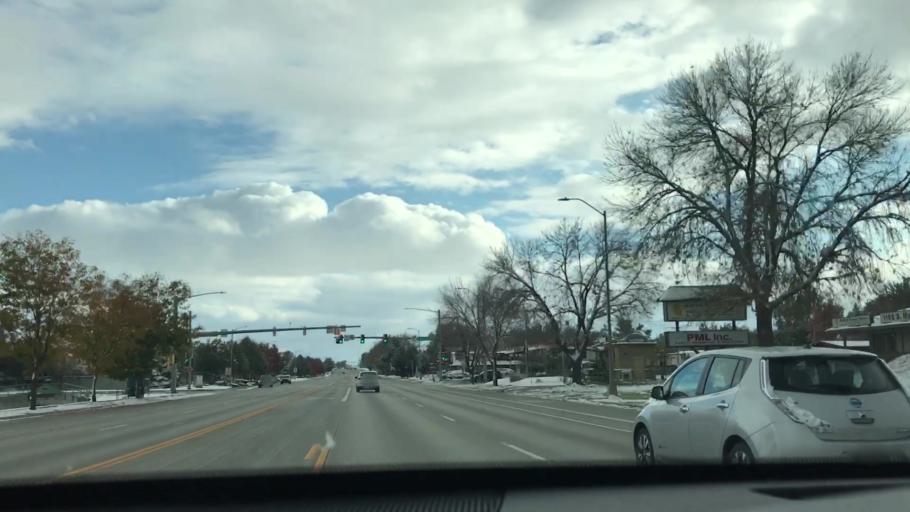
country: US
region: Colorado
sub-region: Boulder County
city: Longmont
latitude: 40.1457
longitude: -105.1028
